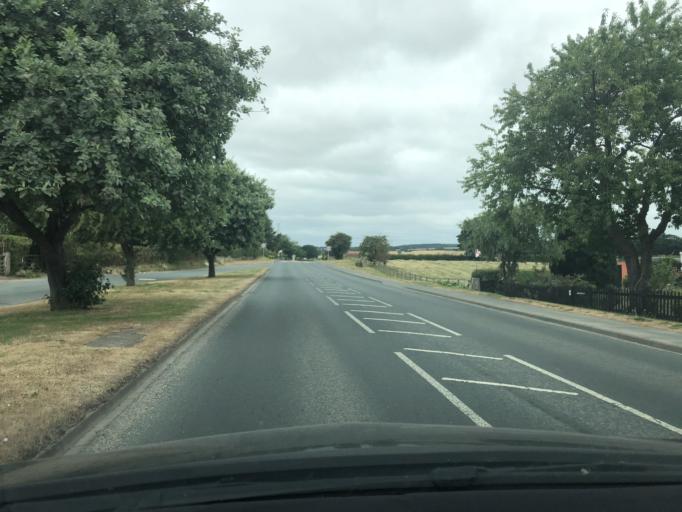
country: GB
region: England
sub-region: North Yorkshire
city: East Ayton
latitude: 54.2430
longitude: -0.4473
